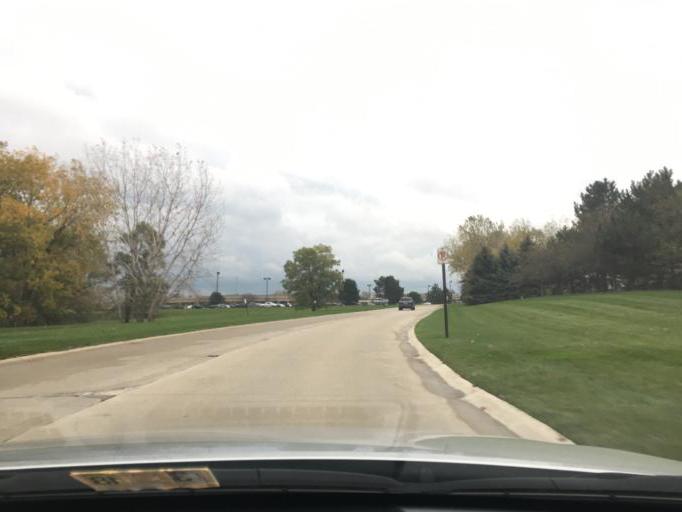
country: US
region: Michigan
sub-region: Wayne County
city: Melvindale
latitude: 42.2957
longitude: -83.1954
